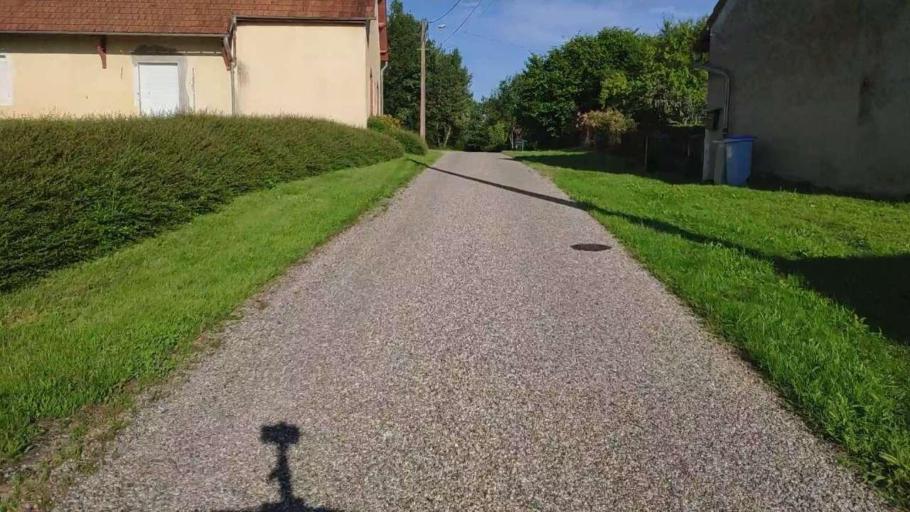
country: FR
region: Franche-Comte
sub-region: Departement du Jura
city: Bletterans
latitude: 46.7949
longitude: 5.4874
